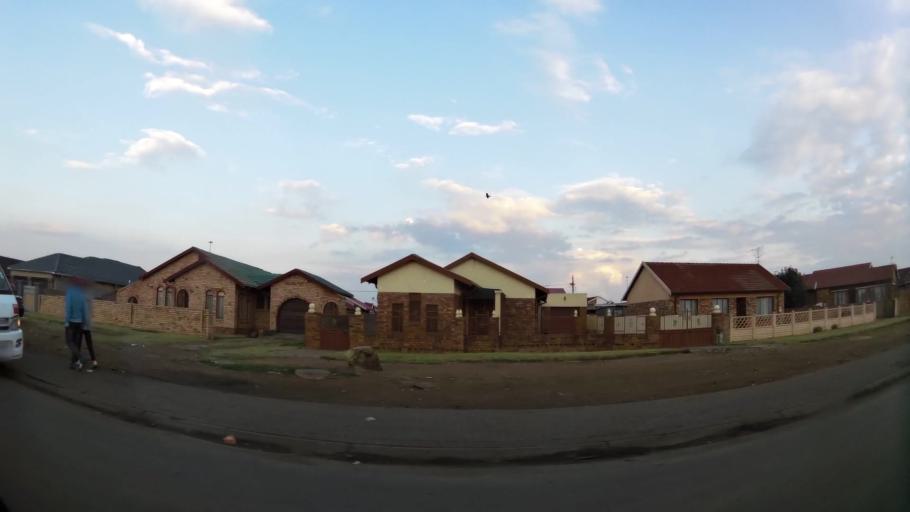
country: ZA
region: Gauteng
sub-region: City of Johannesburg Metropolitan Municipality
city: Orange Farm
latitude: -26.5655
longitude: 27.8500
